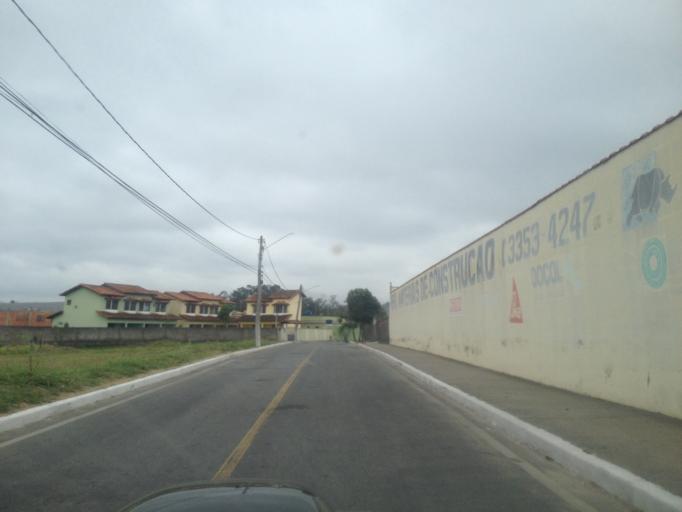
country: BR
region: Rio de Janeiro
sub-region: Porto Real
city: Porto Real
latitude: -22.4140
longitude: -44.3105
